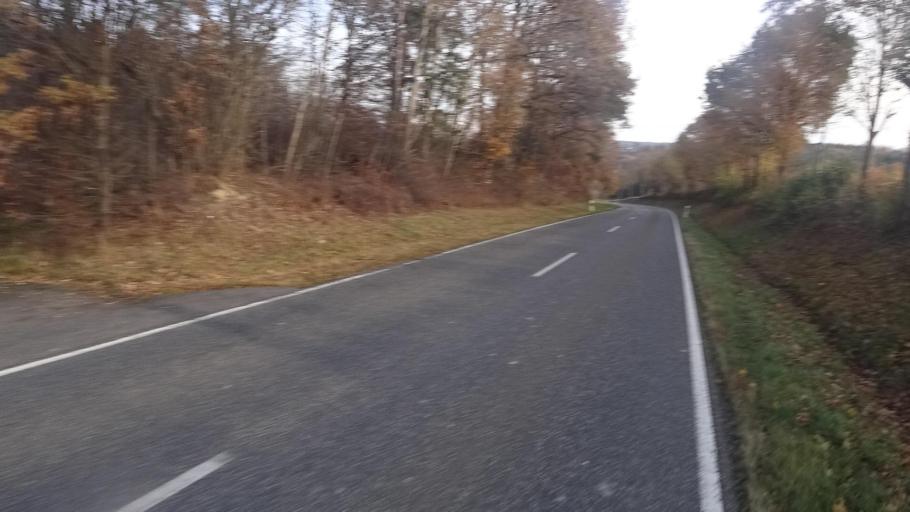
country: DE
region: Rheinland-Pfalz
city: Muhlpfad
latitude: 50.1183
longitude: 7.5595
